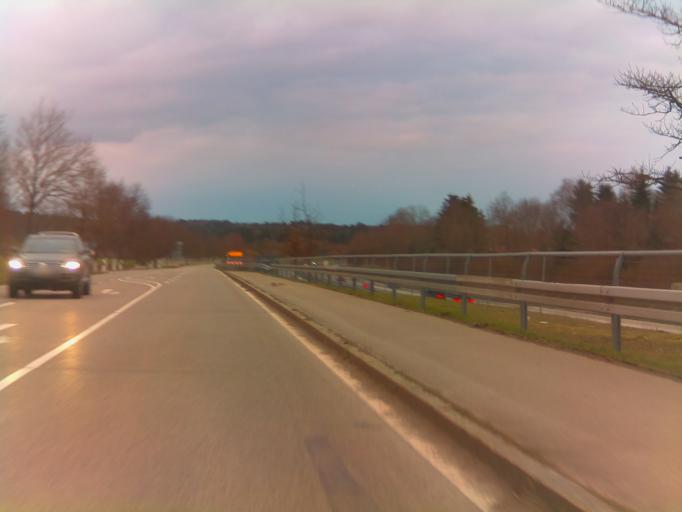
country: DE
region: Bavaria
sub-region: Upper Bavaria
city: Windach
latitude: 48.0742
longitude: 11.0384
